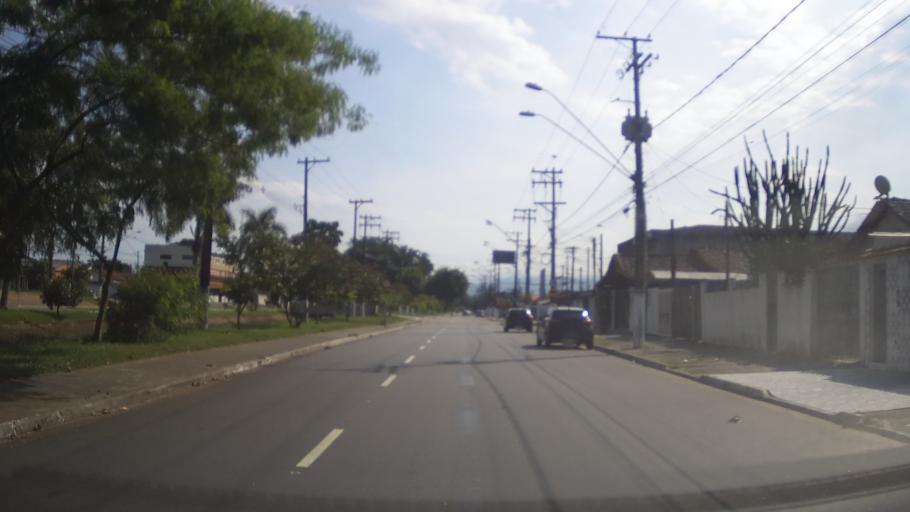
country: BR
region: Sao Paulo
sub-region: Praia Grande
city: Praia Grande
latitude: -24.0009
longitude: -46.4244
